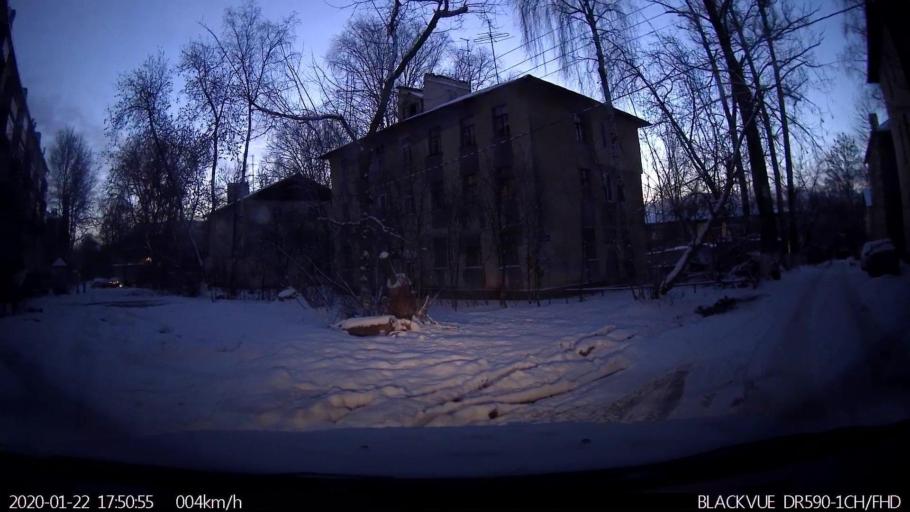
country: RU
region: Nizjnij Novgorod
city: Nizhniy Novgorod
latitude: 56.2923
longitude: 44.0110
